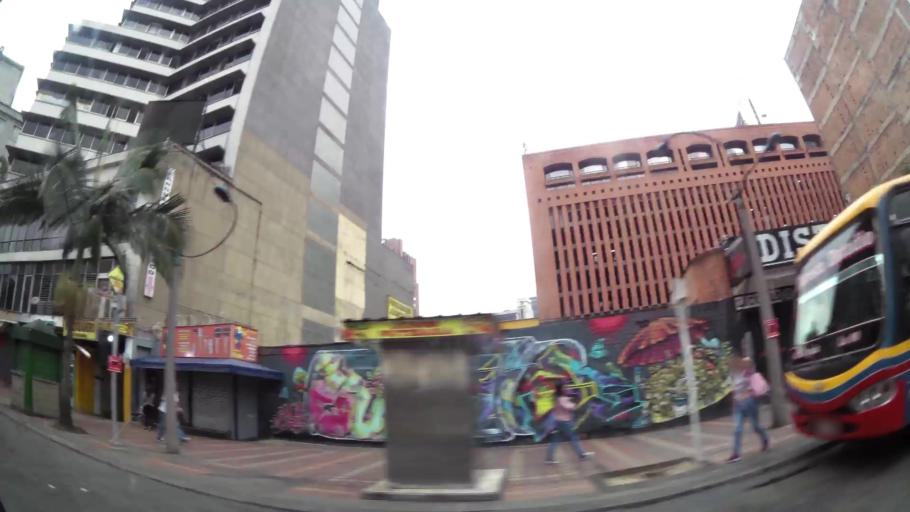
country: CO
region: Antioquia
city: Medellin
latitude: 6.2501
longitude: -75.5657
